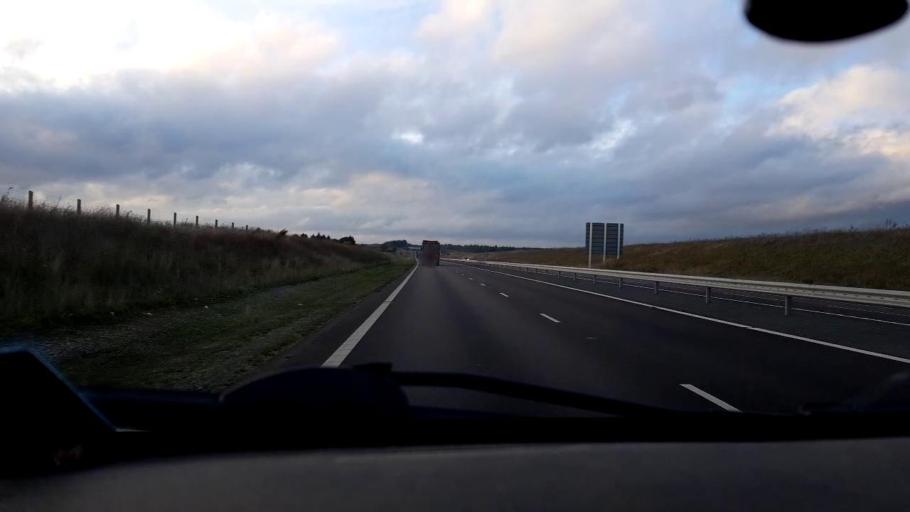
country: GB
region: England
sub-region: Norfolk
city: Horsford
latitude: 52.6877
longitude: 1.2382
